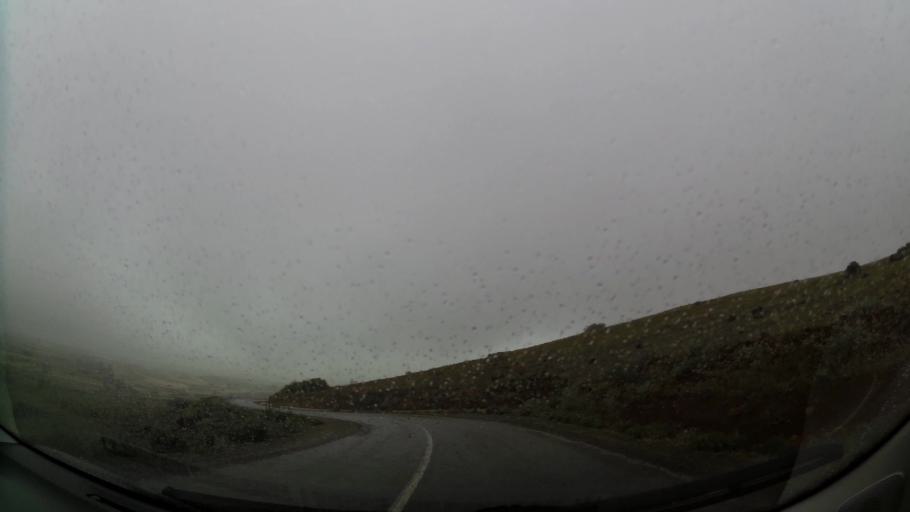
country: MA
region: Oriental
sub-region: Nador
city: Boudinar
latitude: 35.1383
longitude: -3.6051
